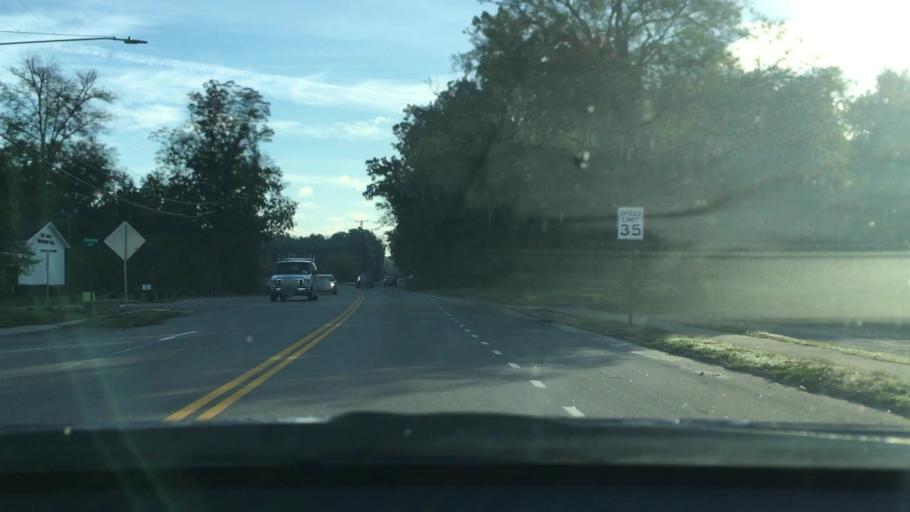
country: US
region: South Carolina
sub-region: Sumter County
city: Sumter
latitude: 33.9247
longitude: -80.3307
